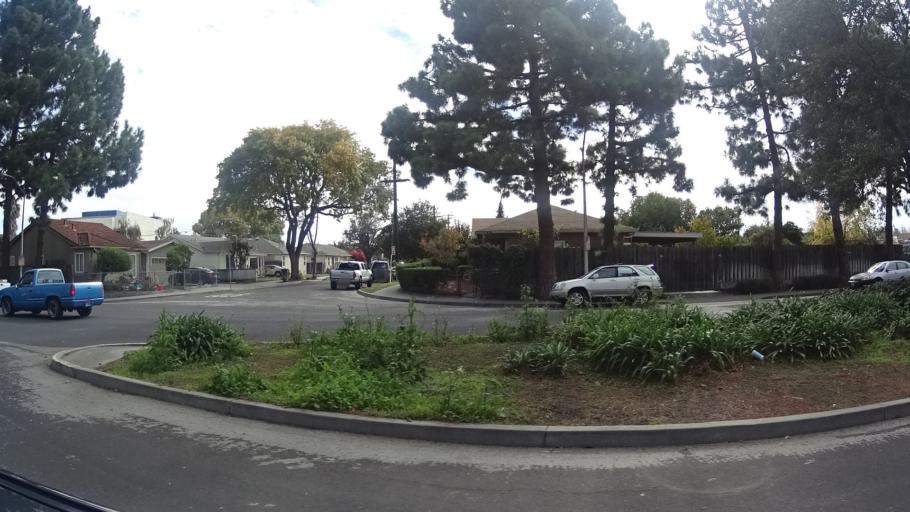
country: US
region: California
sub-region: Santa Clara County
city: Santa Clara
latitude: 37.3626
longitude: -121.9499
